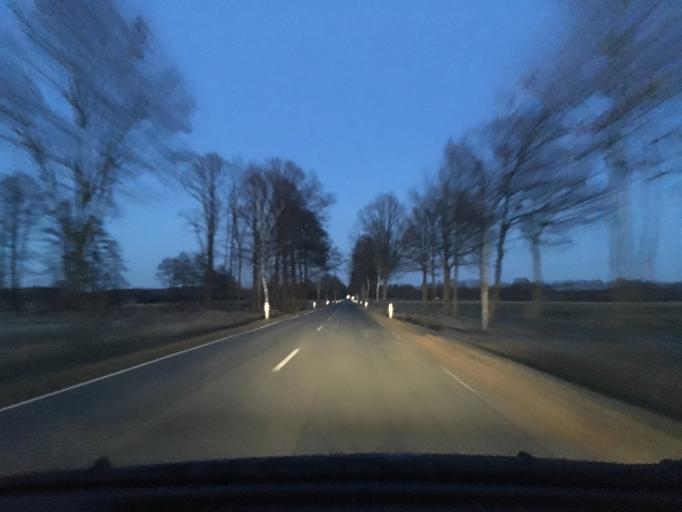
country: DE
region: Lower Saxony
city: Hemslingen
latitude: 53.0979
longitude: 9.6457
